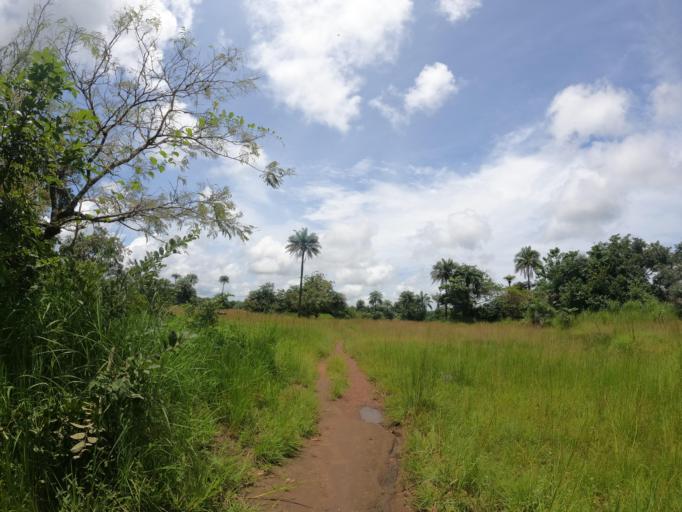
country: SL
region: Northern Province
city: Makeni
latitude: 9.1500
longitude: -12.2546
